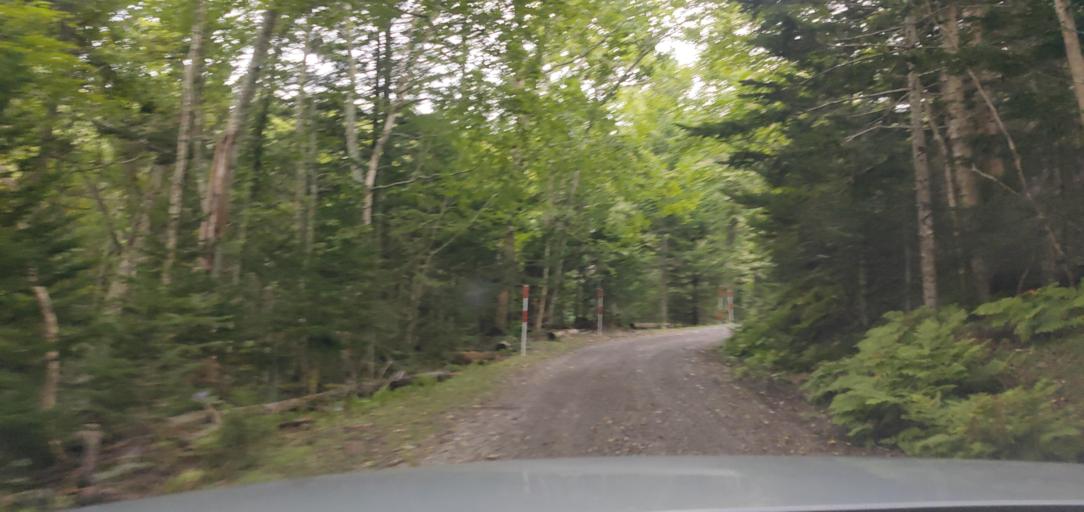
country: JP
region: Hokkaido
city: Kitami
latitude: 43.3700
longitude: 143.9492
